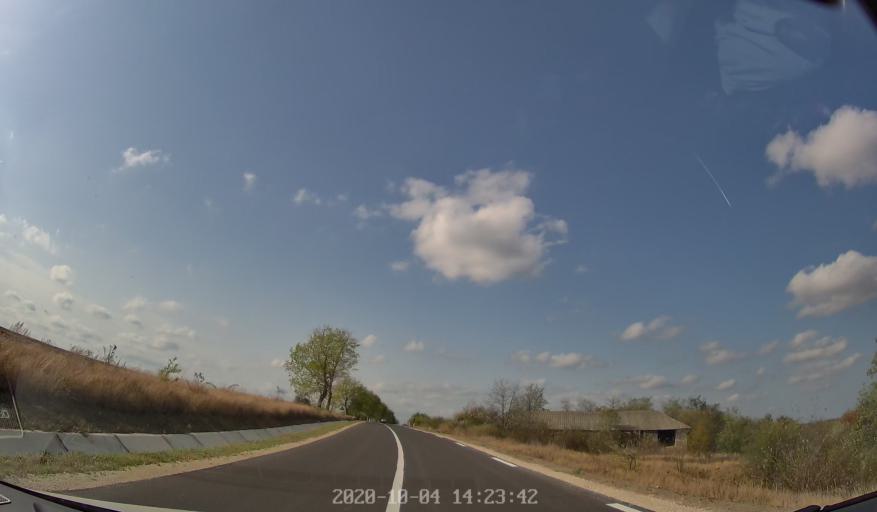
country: MD
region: Rezina
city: Saharna
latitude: 47.6103
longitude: 28.9313
